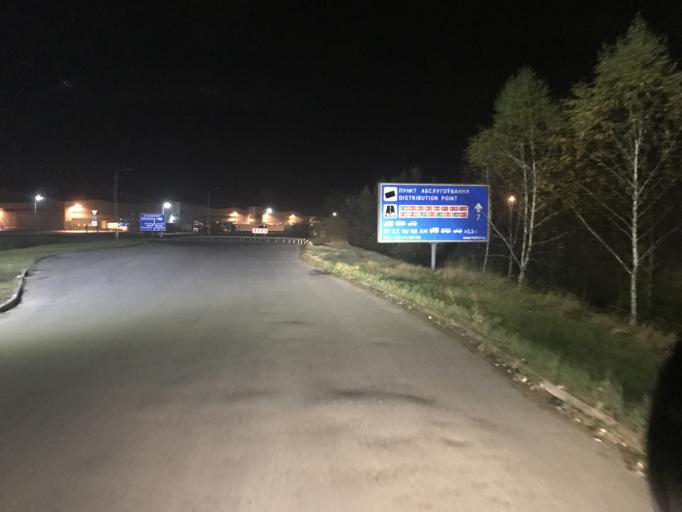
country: PL
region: Lublin Voivodeship
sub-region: Powiat bialski
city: Terespol
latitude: 52.1249
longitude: 23.5798
